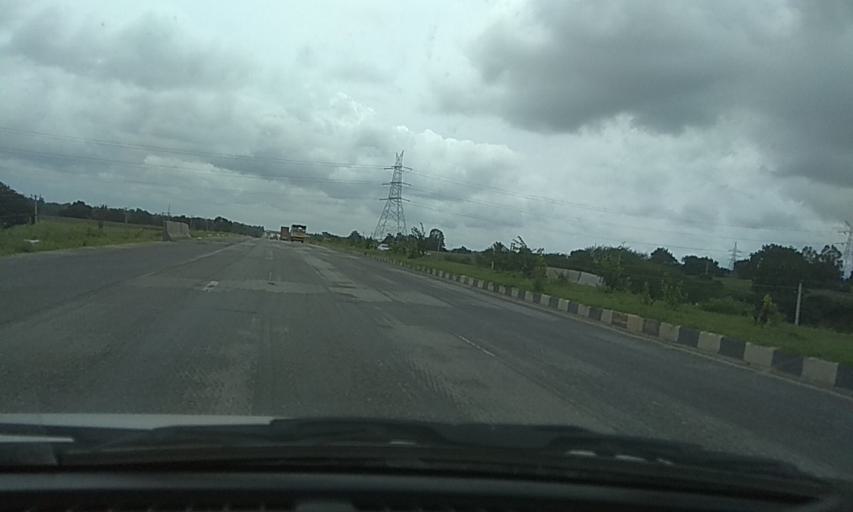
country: IN
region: Karnataka
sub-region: Davanagere
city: Mayakonda
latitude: 14.3697
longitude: 76.1342
